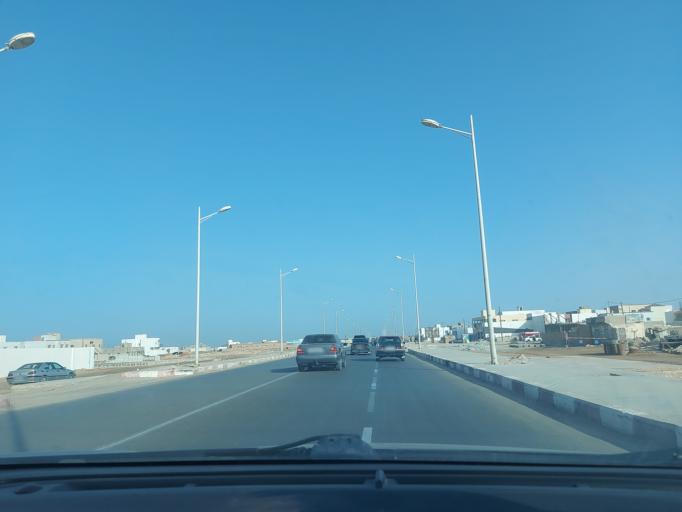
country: MR
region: Nouakchott
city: Nouakchott
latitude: 18.0948
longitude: -16.0152
